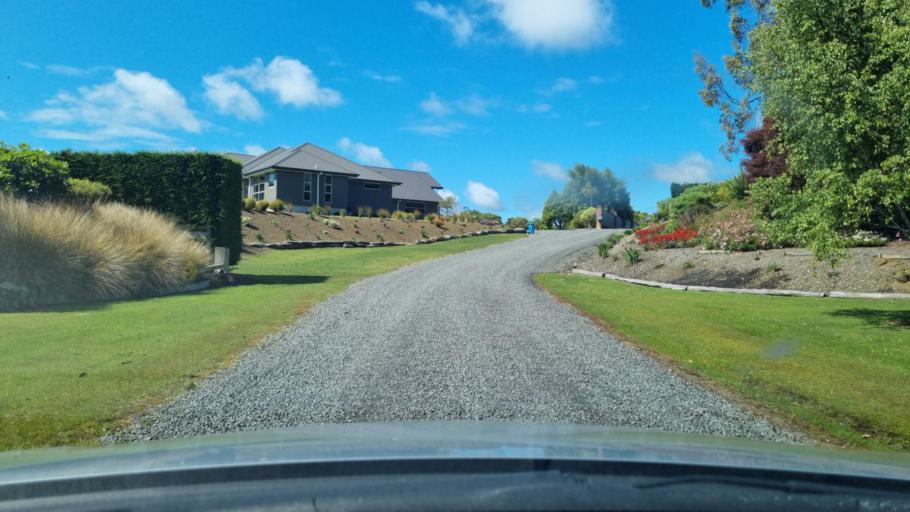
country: NZ
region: Southland
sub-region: Invercargill City
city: Invercargill
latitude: -46.4428
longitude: 168.3196
